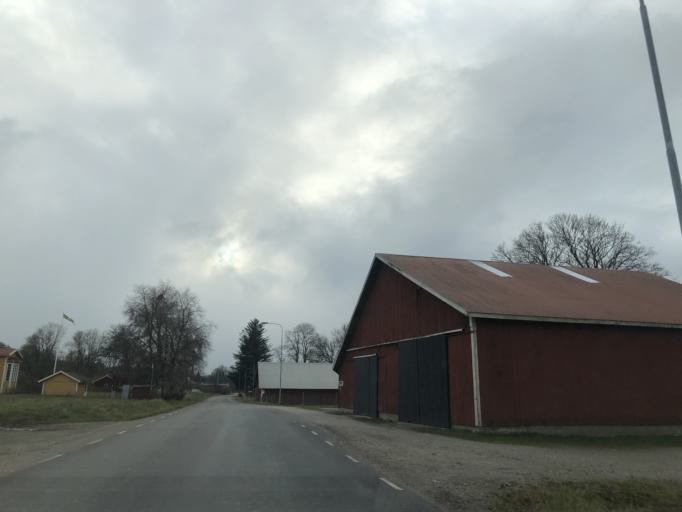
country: SE
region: Vaestra Goetaland
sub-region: Ulricehamns Kommun
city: Ulricehamn
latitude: 57.6853
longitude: 13.4166
